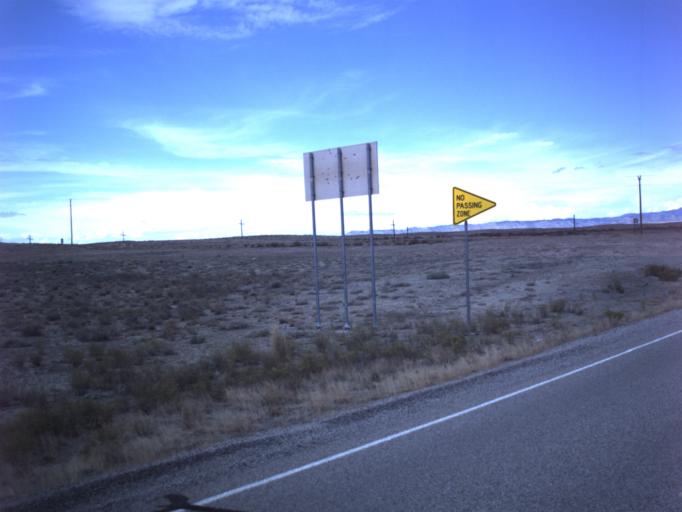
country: US
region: Utah
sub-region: Grand County
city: Moab
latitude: 38.9469
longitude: -109.3553
